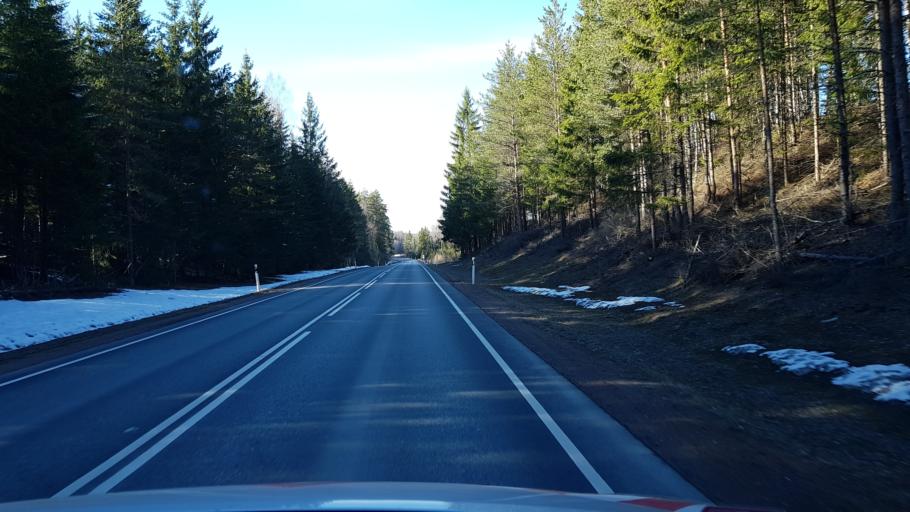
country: EE
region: Laeaene-Virumaa
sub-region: Tapa vald
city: Tapa
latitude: 59.4094
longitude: 26.0019
